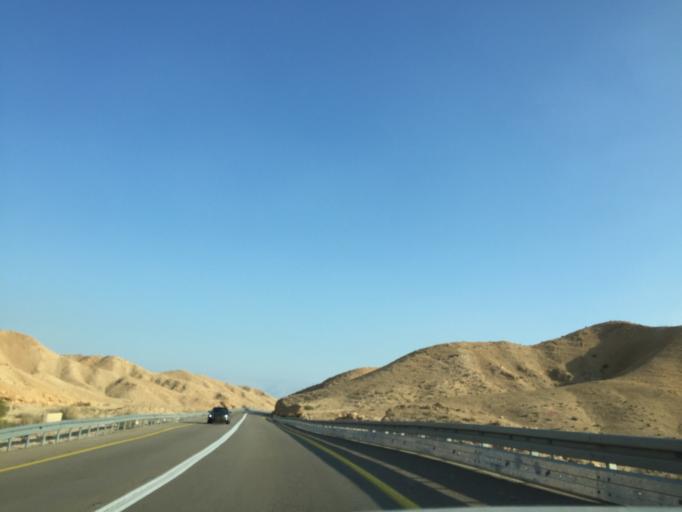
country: IL
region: Southern District
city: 'Arad
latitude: 31.1966
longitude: 35.2708
